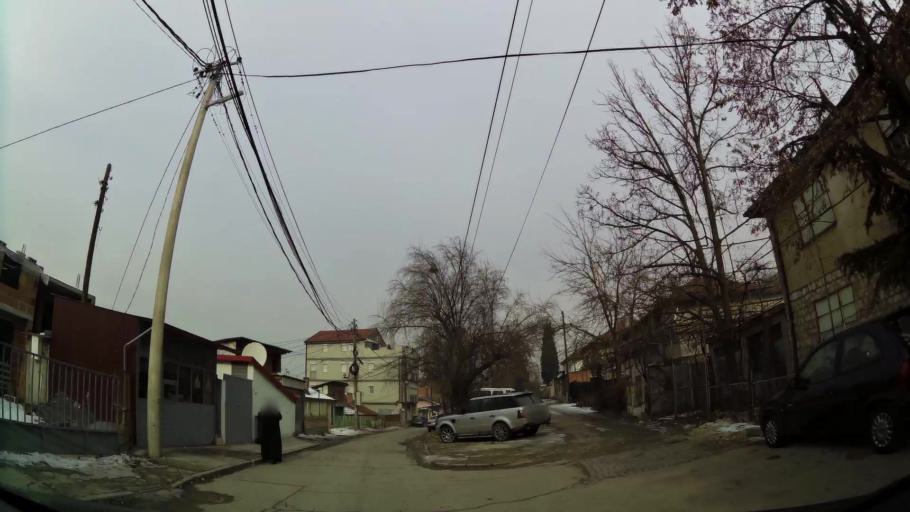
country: MK
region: Cair
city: Cair
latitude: 42.0067
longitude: 21.4469
